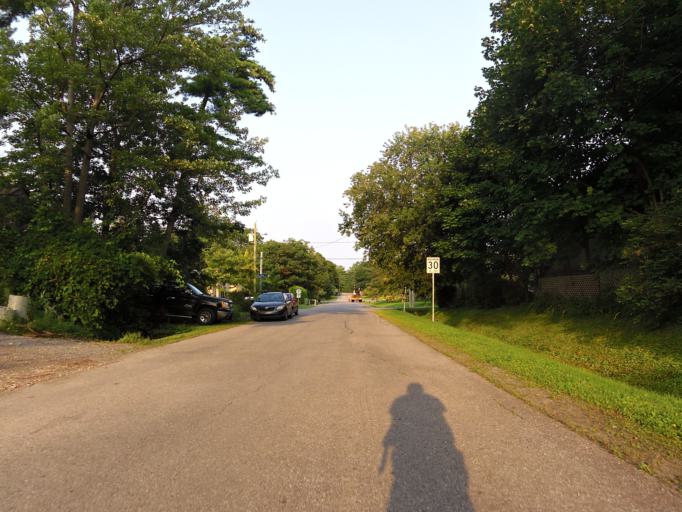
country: CA
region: Ontario
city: Bells Corners
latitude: 45.3868
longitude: -75.8428
